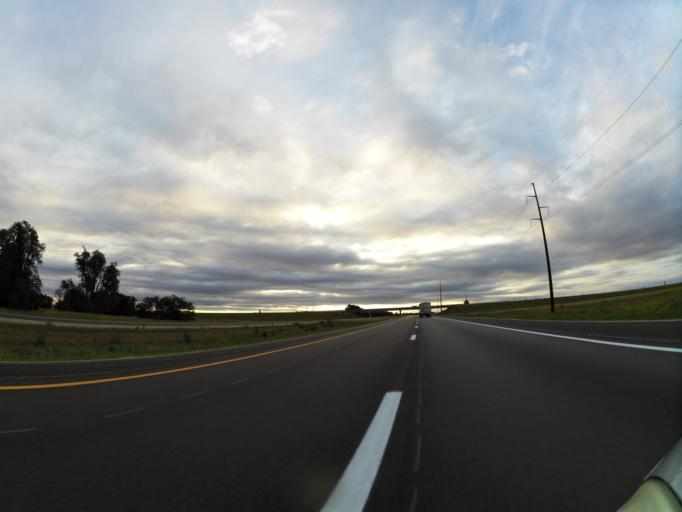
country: US
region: Kansas
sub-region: Reno County
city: South Hutchinson
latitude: 38.0132
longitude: -97.9715
